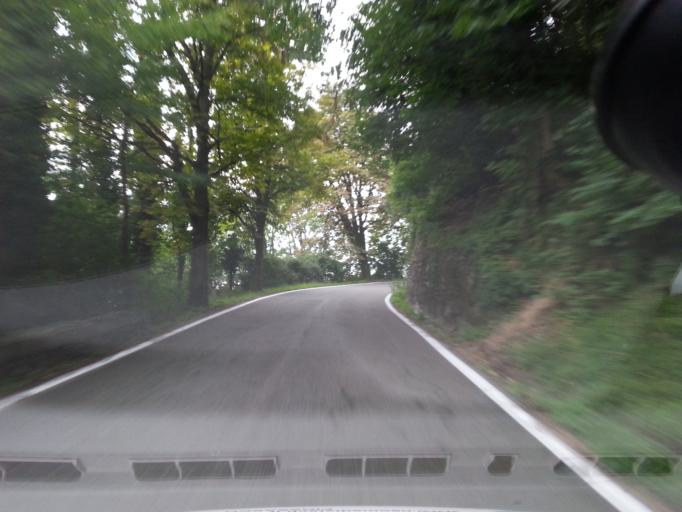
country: IT
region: Piedmont
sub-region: Provincia di Torino
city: Sant'Ambrogio di Torino
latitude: 45.0801
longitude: 7.3592
